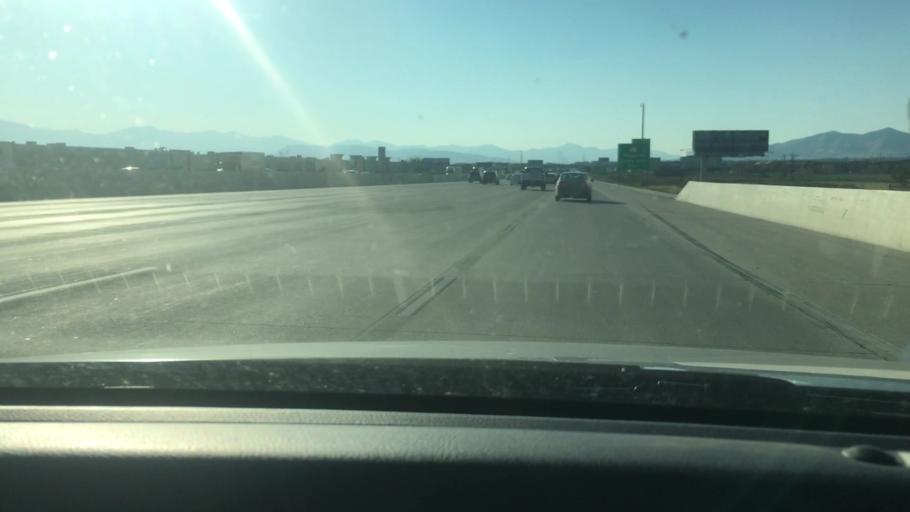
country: US
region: Utah
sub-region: Utah County
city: Lindon
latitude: 40.3372
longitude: -111.7485
